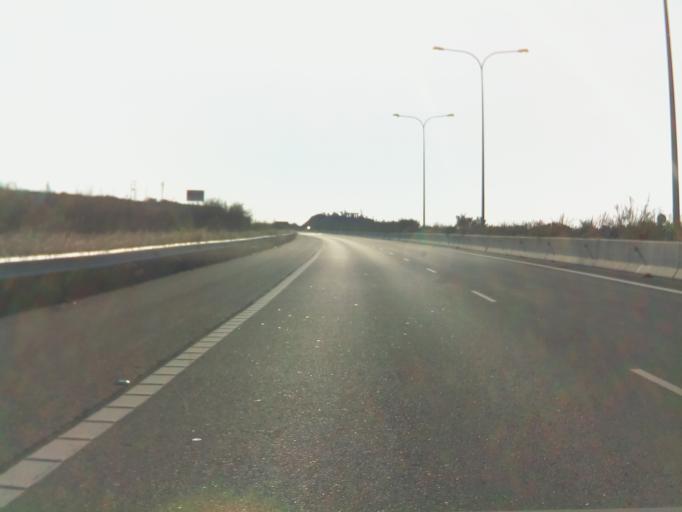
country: CY
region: Limassol
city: Pissouri
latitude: 34.6909
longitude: 32.5789
